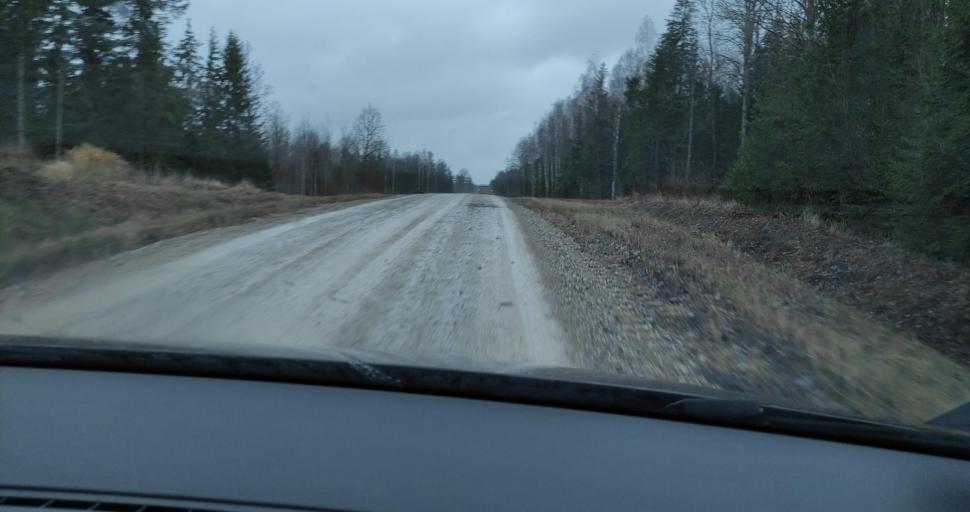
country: LV
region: Skrunda
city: Skrunda
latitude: 56.5692
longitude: 22.1348
